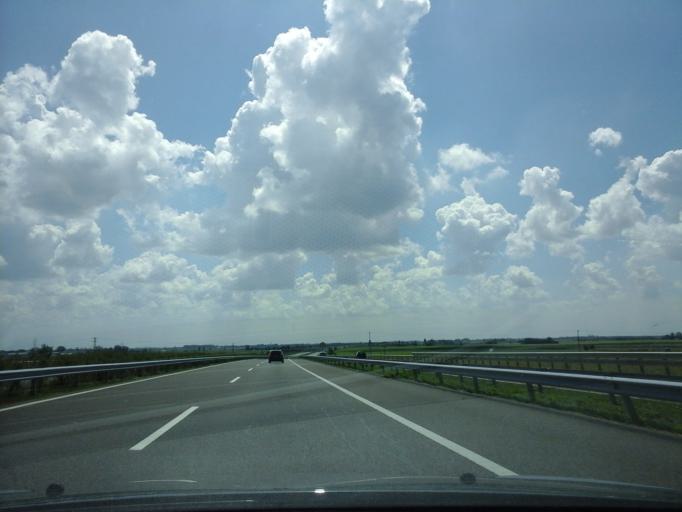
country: HU
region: Hajdu-Bihar
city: Debrecen
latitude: 47.5475
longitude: 21.5523
